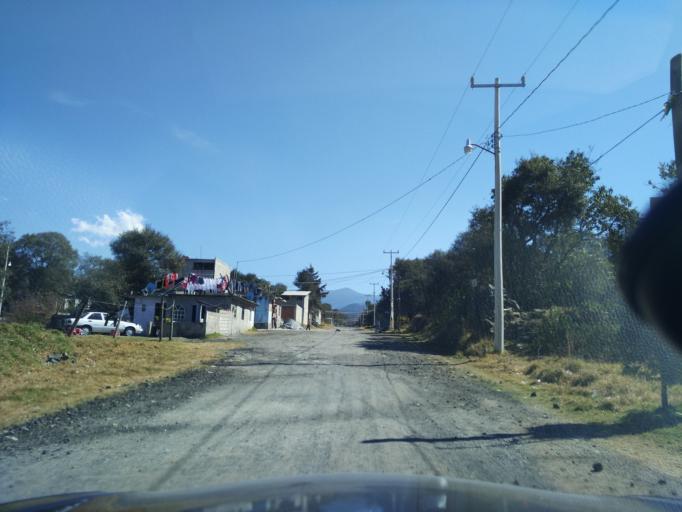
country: MX
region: Mexico
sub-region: Ocoyoacac
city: Colonia el Pirame
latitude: 19.2466
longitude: -99.4689
